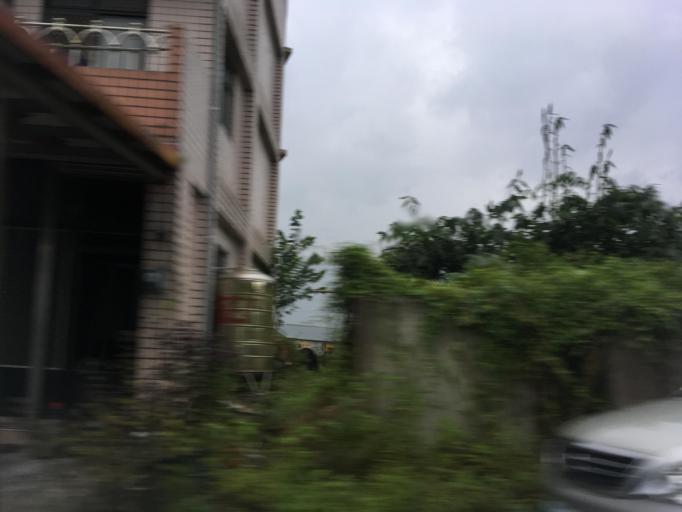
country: TW
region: Taiwan
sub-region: Yilan
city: Yilan
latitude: 24.6771
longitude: 121.6538
